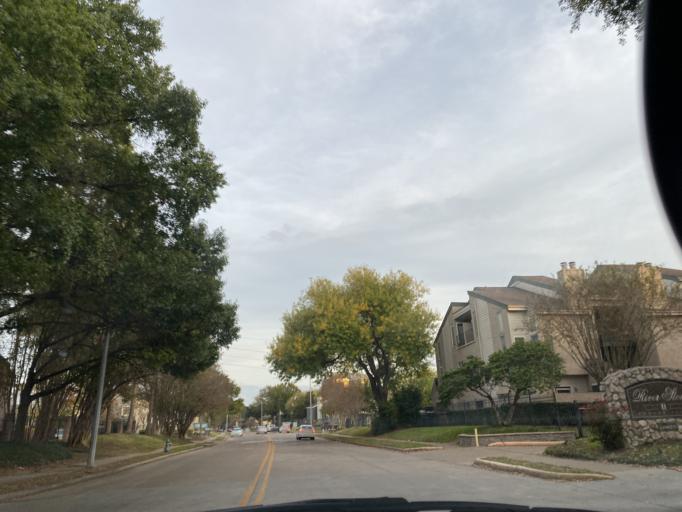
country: US
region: Texas
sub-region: Harris County
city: Bunker Hill Village
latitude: 29.7321
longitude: -95.5664
